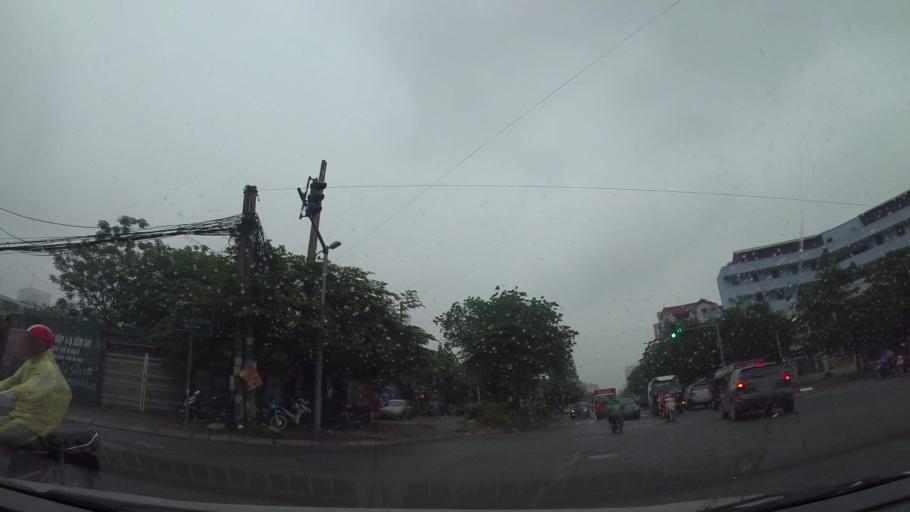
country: VN
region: Ha Noi
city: Cau Giay
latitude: 21.0144
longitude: 105.7958
